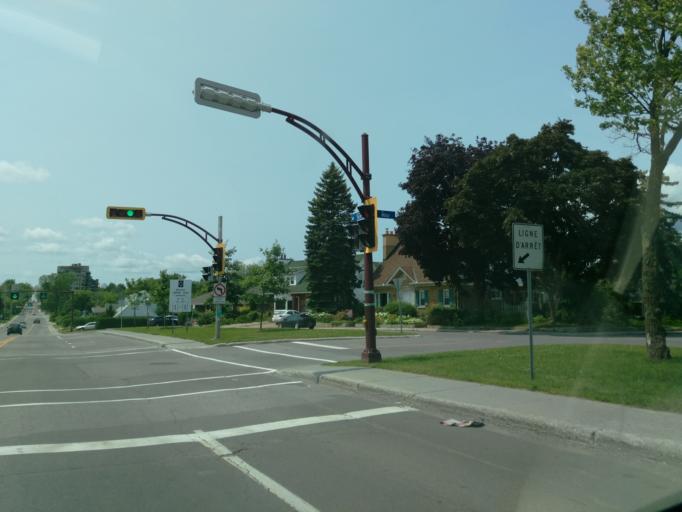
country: CA
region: Ontario
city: Ottawa
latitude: 45.4239
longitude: -75.7285
